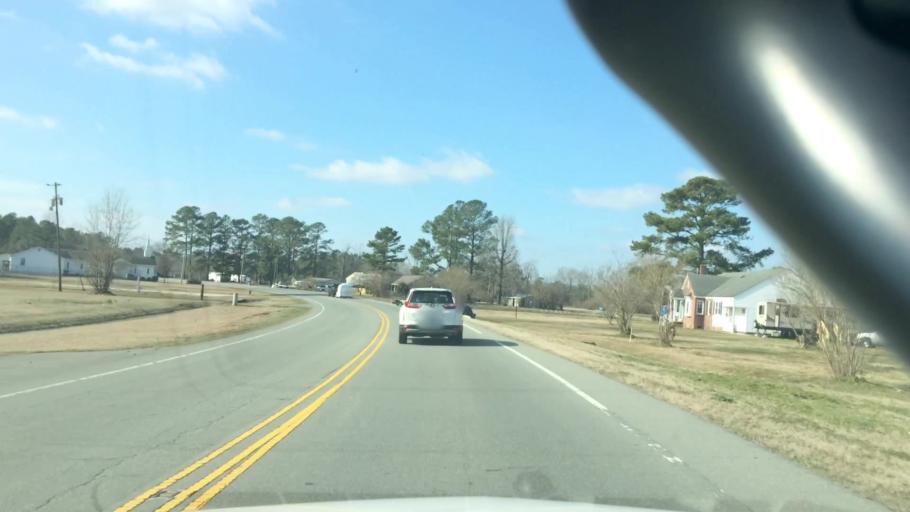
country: US
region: North Carolina
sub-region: Duplin County
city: Beulaville
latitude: 34.8336
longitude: -77.8234
